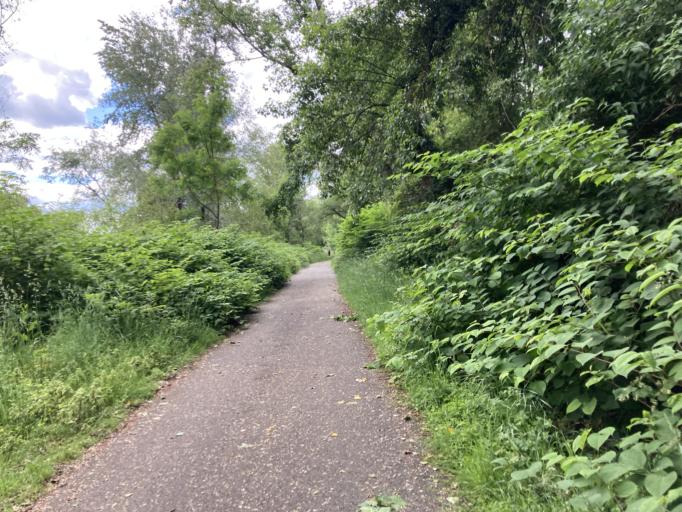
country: FR
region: Aquitaine
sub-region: Departement des Pyrenees-Atlantiques
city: Artiguelouve
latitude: 43.3205
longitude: -0.4551
